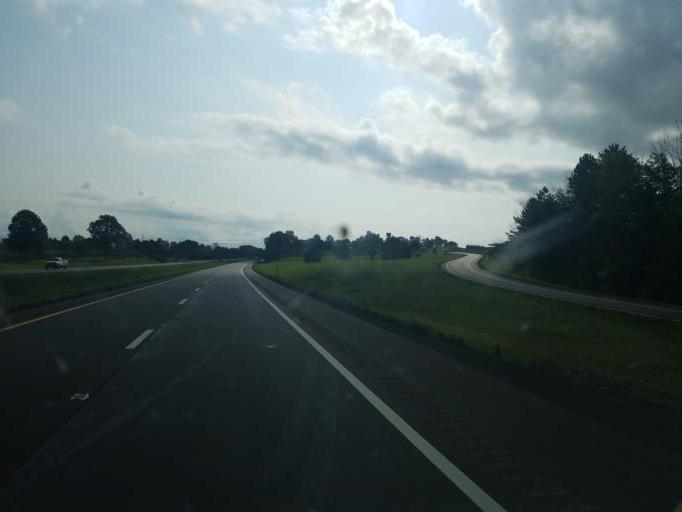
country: US
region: Ohio
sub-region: Ashland County
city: Ashland
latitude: 40.7854
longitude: -82.2665
